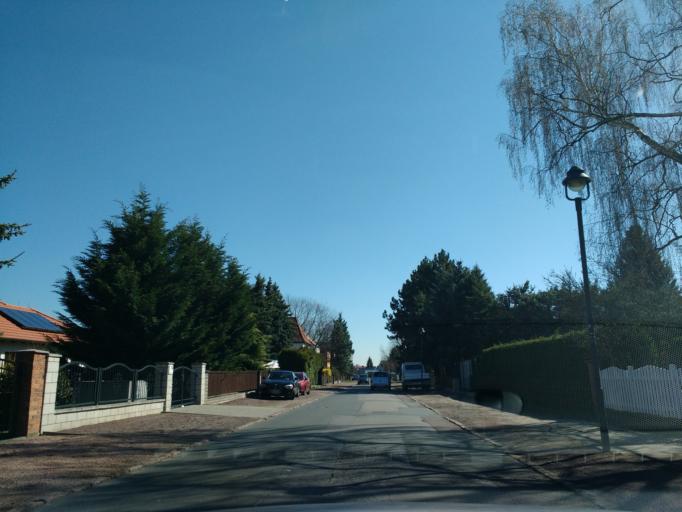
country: DE
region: Saxony-Anhalt
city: Halle (Saale)
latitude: 51.4972
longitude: 12.0213
